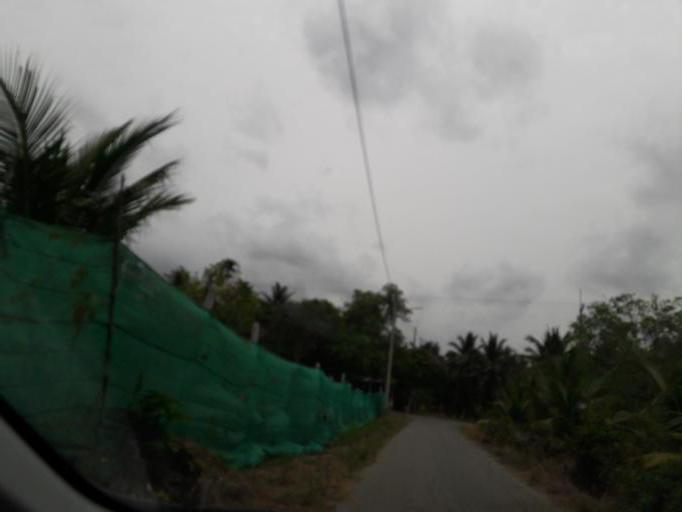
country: TH
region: Samut Sakhon
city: Ban Phaeo
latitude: 13.6141
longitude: 100.0227
